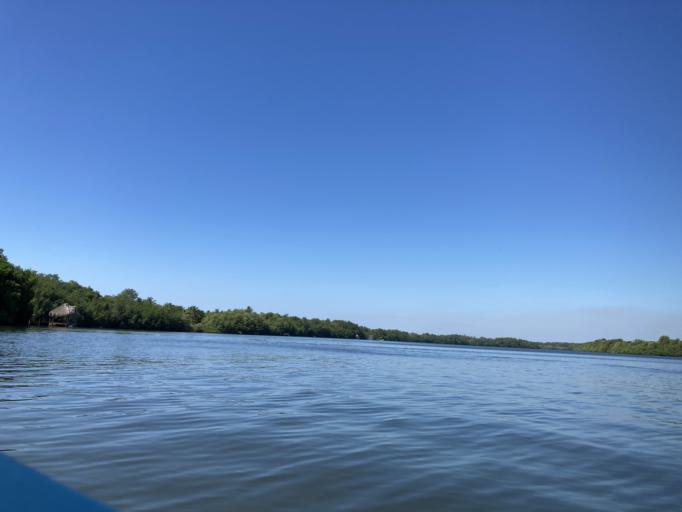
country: GT
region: Jutiapa
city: Pasaco
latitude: 13.8096
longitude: -90.2795
